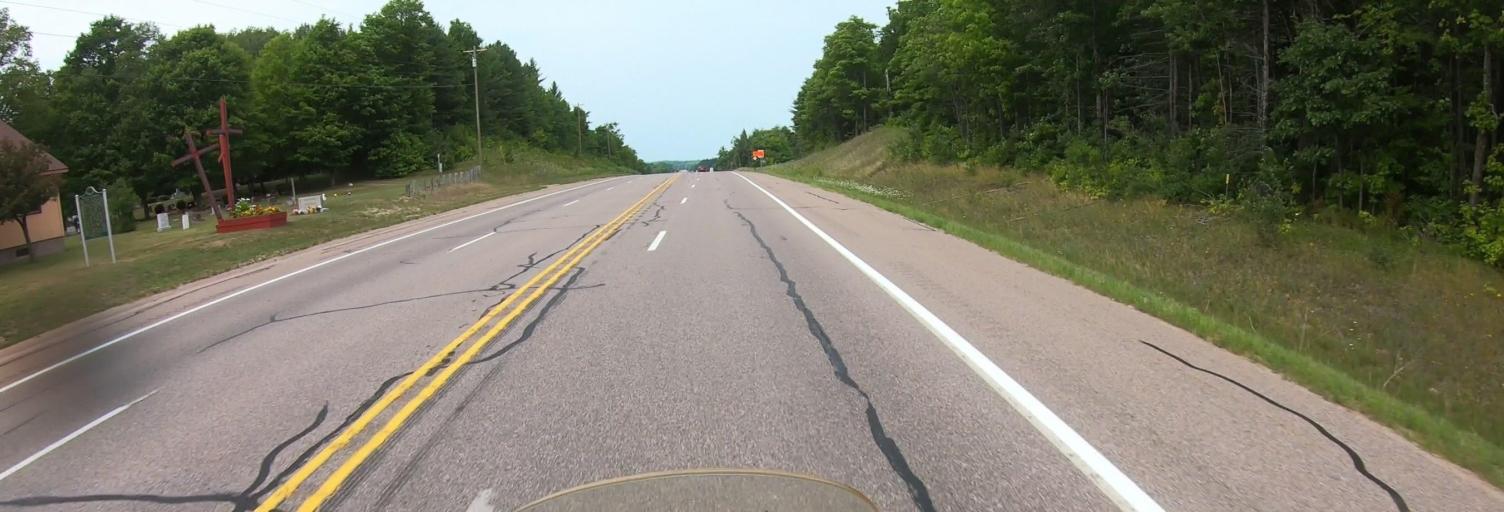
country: US
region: Michigan
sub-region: Marquette County
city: K. I. Sawyer Air Force Base
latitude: 46.3529
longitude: -87.2204
